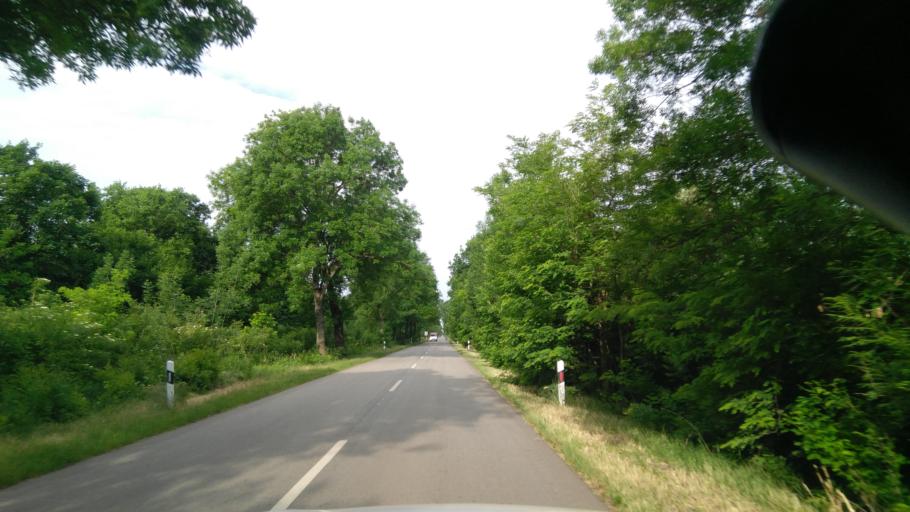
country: HU
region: Bekes
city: Ketegyhaza
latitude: 46.5377
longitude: 21.1400
